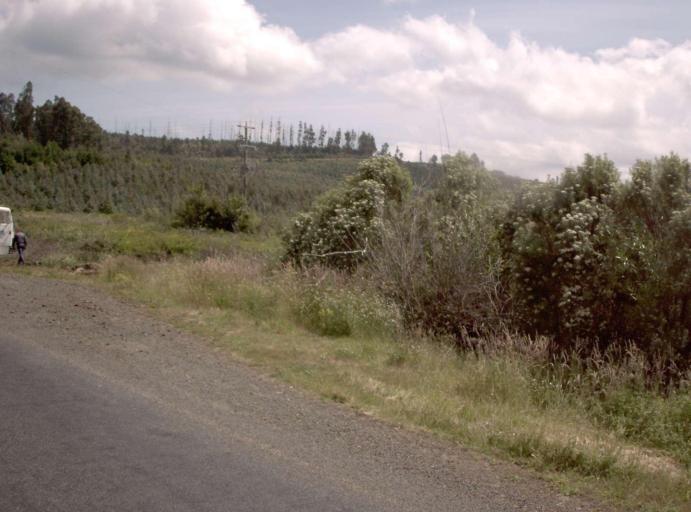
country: AU
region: Victoria
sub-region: Latrobe
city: Traralgon
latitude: -38.3553
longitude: 146.5694
